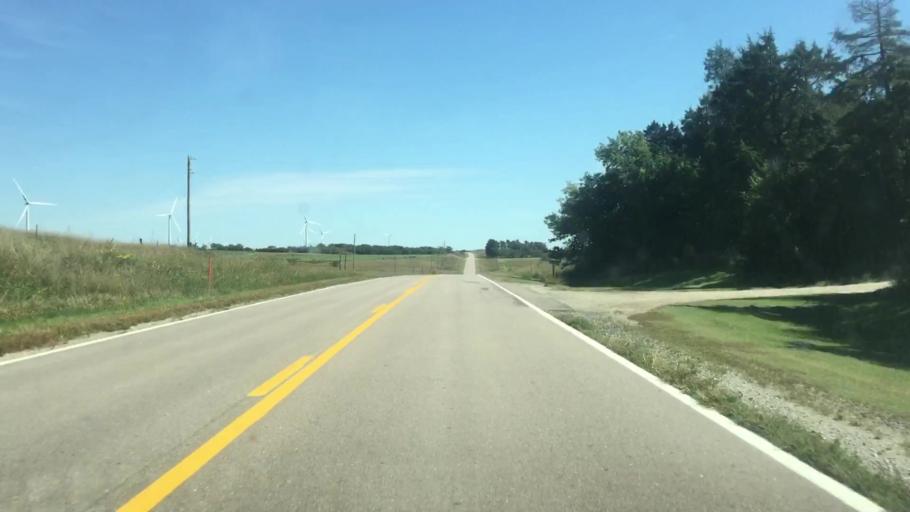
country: US
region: Nebraska
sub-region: Jefferson County
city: Fairbury
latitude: 40.0451
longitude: -96.9834
